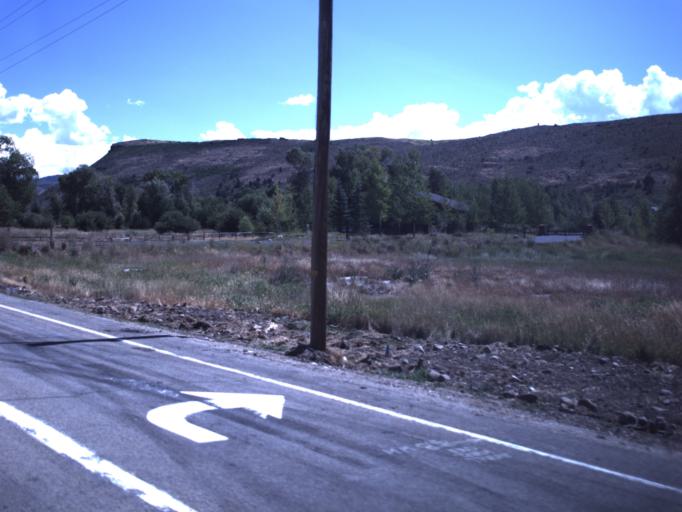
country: US
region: Utah
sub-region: Summit County
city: Francis
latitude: 40.6062
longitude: -111.3156
